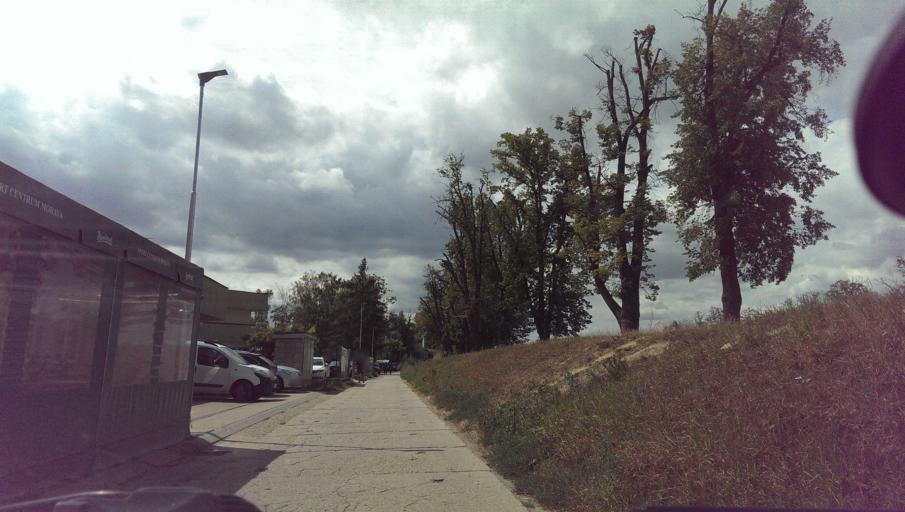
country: CZ
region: Zlin
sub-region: Okres Uherske Hradiste
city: Uherske Hradiste
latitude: 49.0751
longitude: 17.4744
